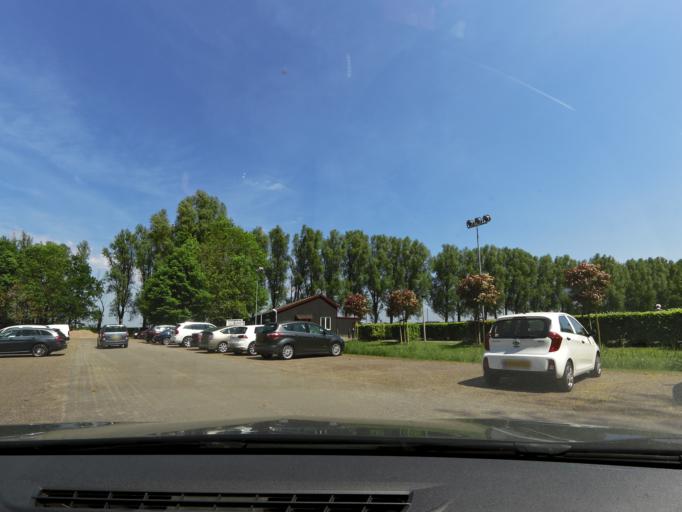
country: NL
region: South Holland
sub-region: Gemeente Binnenmaas
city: Heinenoord
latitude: 51.8357
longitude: 4.4612
